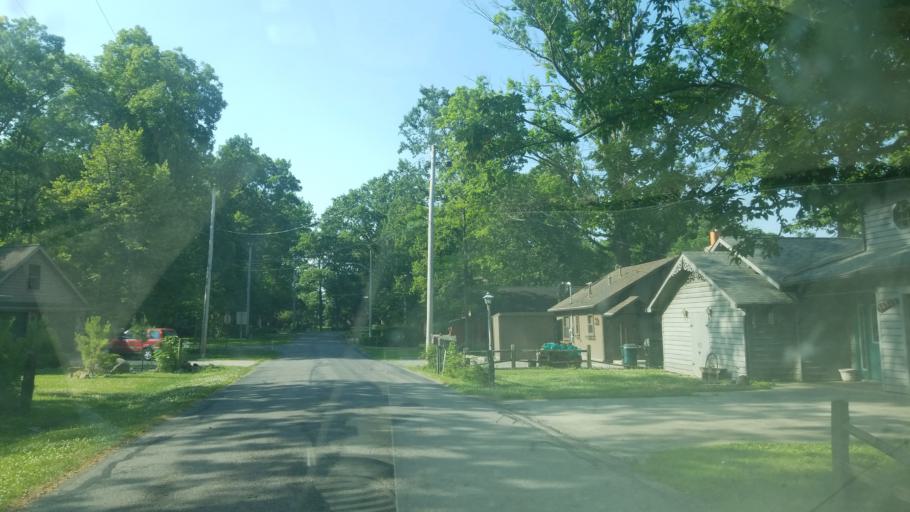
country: US
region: Ohio
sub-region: Logan County
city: Russells Point
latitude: 40.4974
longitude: -83.8746
